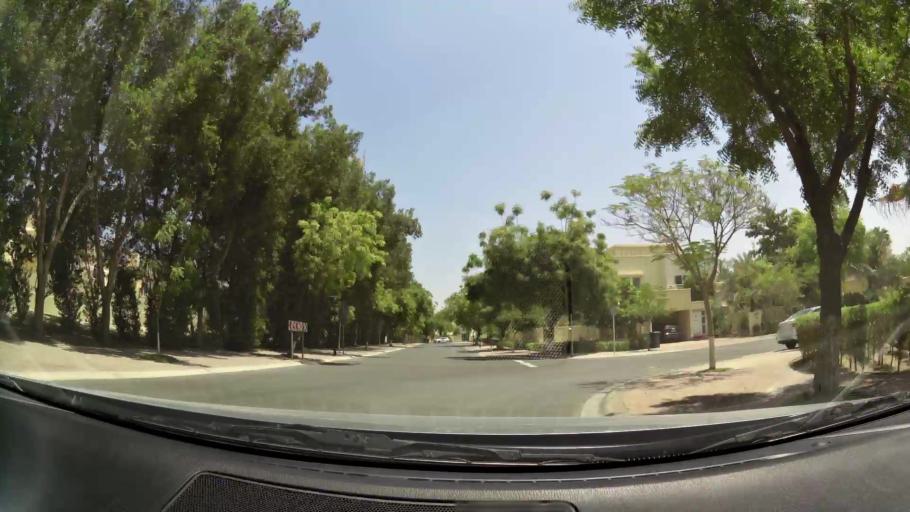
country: AE
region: Dubai
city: Dubai
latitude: 25.0476
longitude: 55.1723
